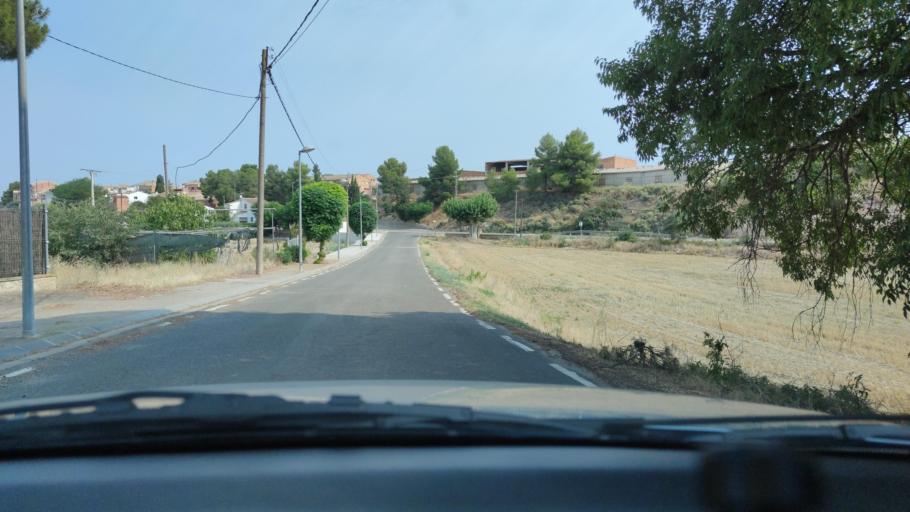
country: ES
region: Catalonia
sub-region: Provincia de Lleida
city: Arbeca
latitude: 41.5067
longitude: 0.9225
